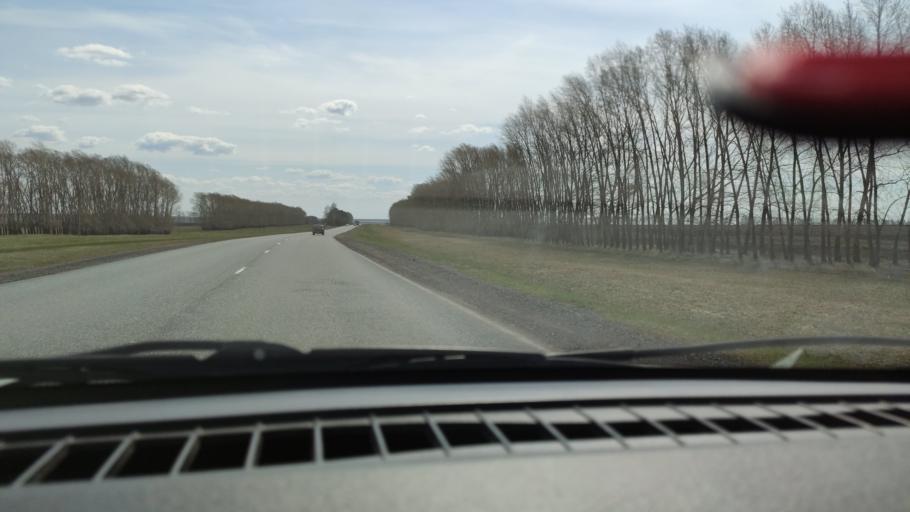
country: RU
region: Bashkortostan
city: Kushnarenkovo
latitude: 55.1846
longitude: 55.1252
